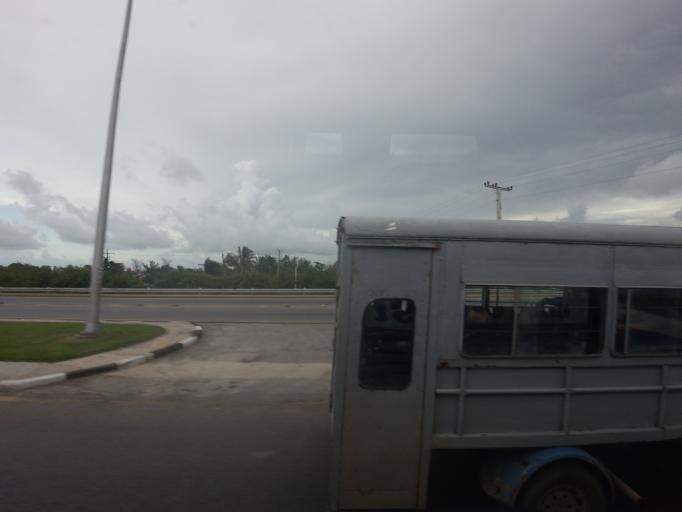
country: CU
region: Matanzas
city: Varadero
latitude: 23.1325
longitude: -81.2834
